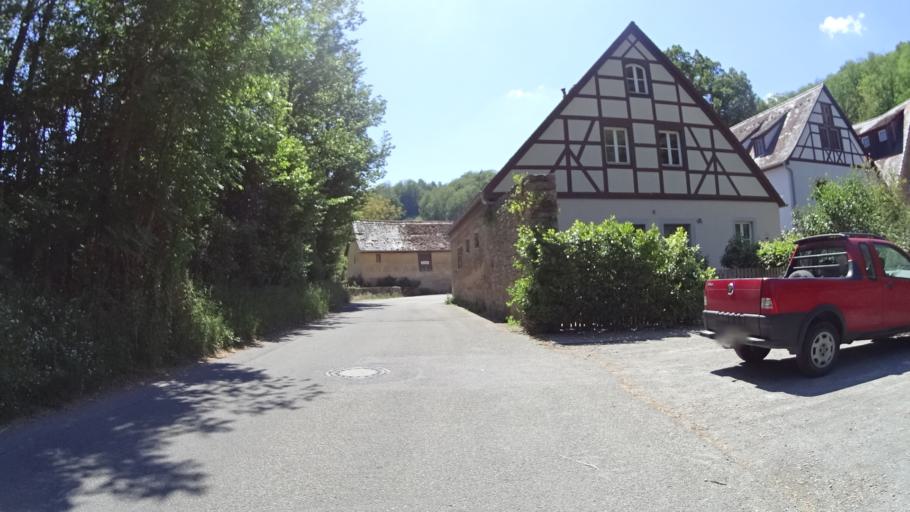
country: DE
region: Bavaria
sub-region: Regierungsbezirk Mittelfranken
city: Rothenburg ob der Tauber
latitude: 49.3769
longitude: 10.1697
